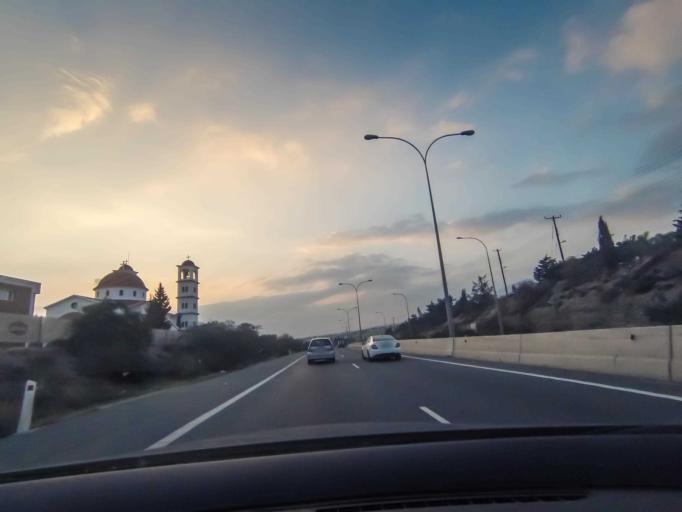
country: CY
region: Limassol
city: Mouttagiaka
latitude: 34.7062
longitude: 33.0985
